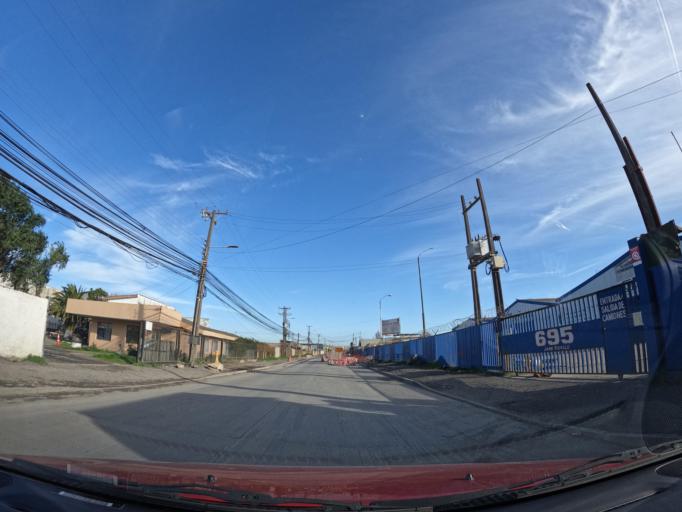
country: CL
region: Biobio
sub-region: Provincia de Concepcion
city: Talcahuano
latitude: -36.7633
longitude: -73.0814
